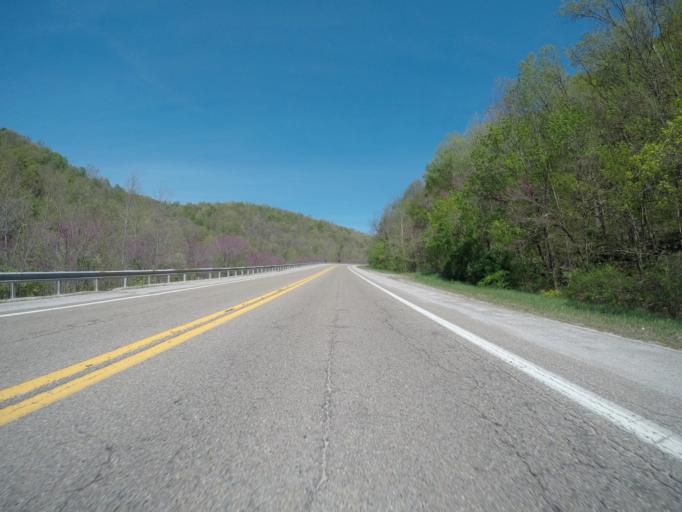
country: US
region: West Virginia
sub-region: Kanawha County
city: Charleston
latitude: 38.4128
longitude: -81.6406
